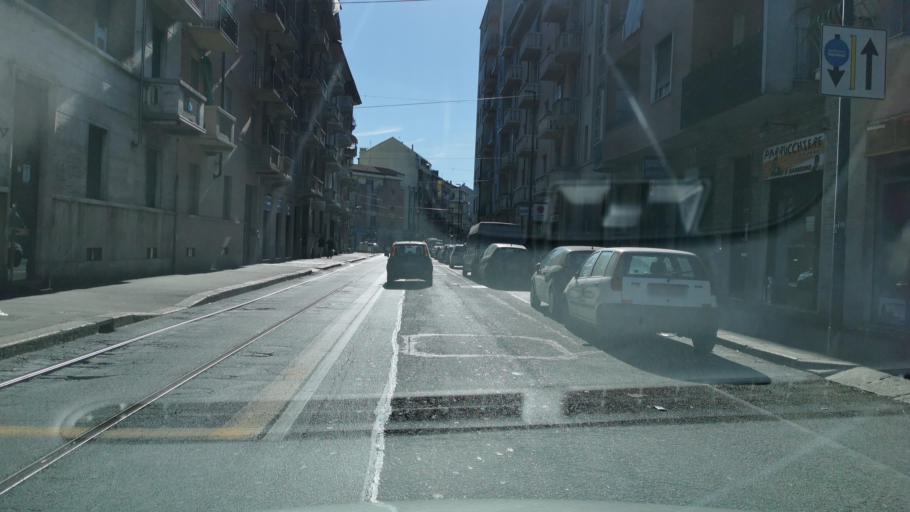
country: IT
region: Piedmont
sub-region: Provincia di Torino
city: Turin
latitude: 45.0998
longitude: 7.6807
